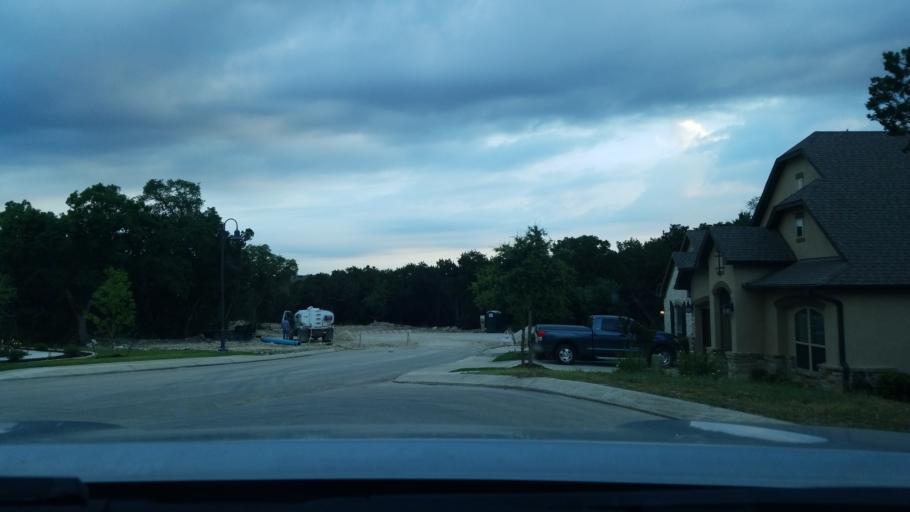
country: US
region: Texas
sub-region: Bexar County
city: Timberwood Park
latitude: 29.7173
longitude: -98.4575
